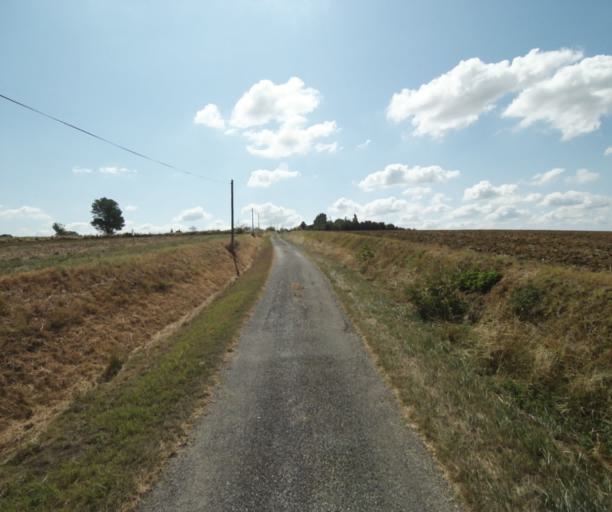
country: FR
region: Midi-Pyrenees
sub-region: Departement de la Haute-Garonne
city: Auriac-sur-Vendinelle
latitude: 43.4521
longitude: 1.7845
